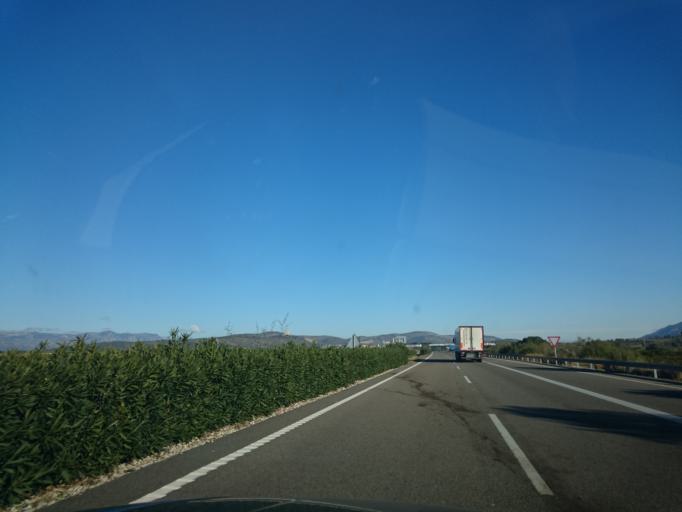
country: ES
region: Catalonia
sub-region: Provincia de Tarragona
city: Ulldecona
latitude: 40.5597
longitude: 0.4279
